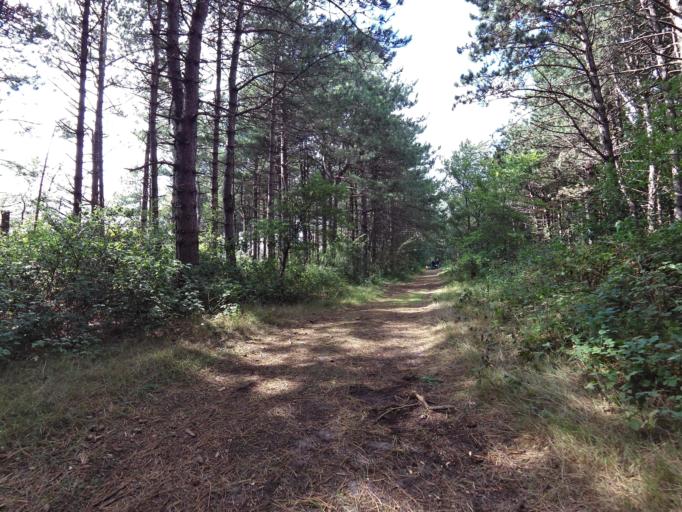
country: NL
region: South Holland
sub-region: Gemeente Goeree-Overflakkee
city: Ouddorp
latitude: 51.8266
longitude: 3.9518
